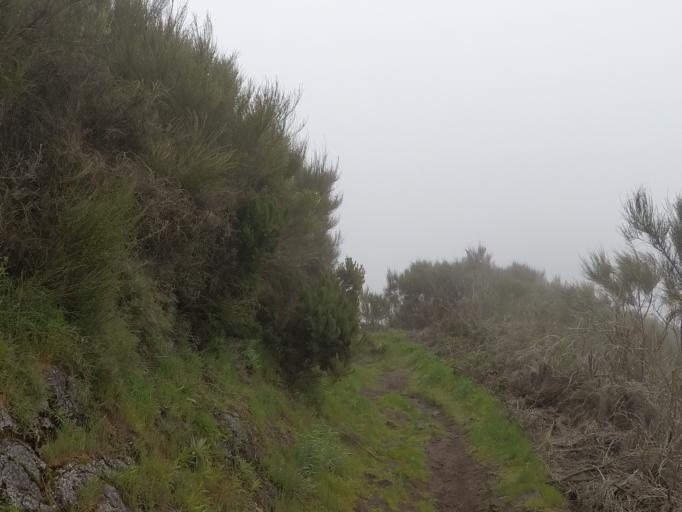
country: PT
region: Madeira
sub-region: Camara de Lobos
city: Curral das Freiras
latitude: 32.7244
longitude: -16.9882
